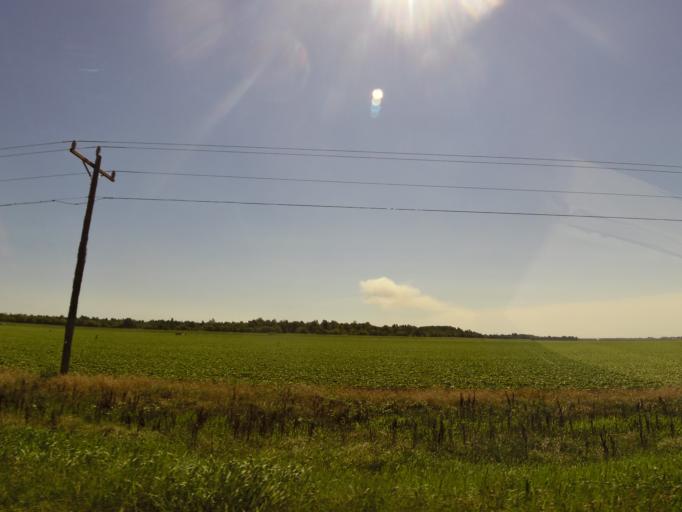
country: US
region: Arkansas
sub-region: Clay County
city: Piggott
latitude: 36.4136
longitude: -90.1476
